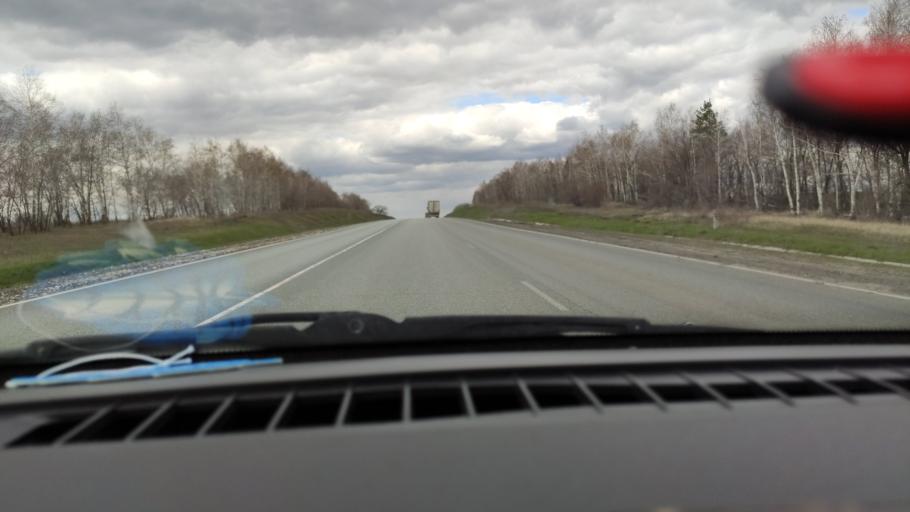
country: RU
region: Saratov
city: Tersa
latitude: 52.1029
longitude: 47.4981
